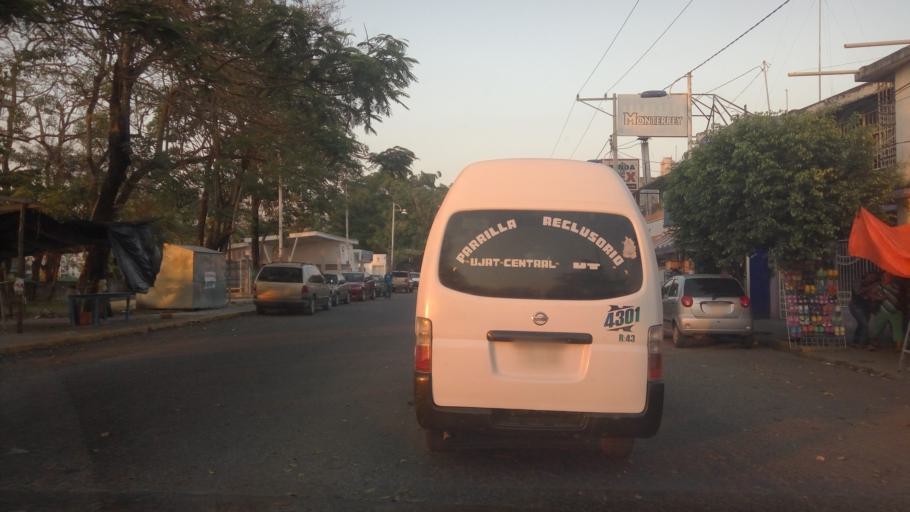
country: MX
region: Tabasco
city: Villahermosa
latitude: 17.9846
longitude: -92.9187
